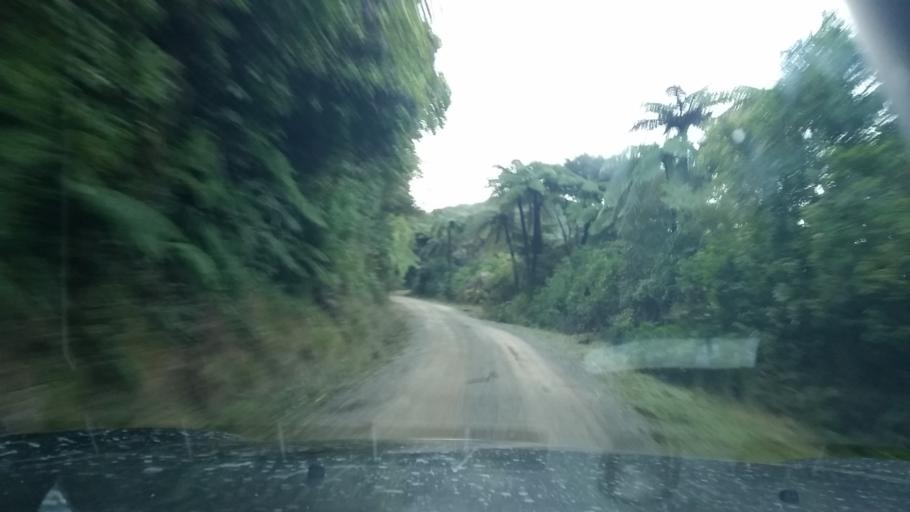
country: NZ
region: Marlborough
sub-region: Marlborough District
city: Picton
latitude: -41.1312
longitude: 174.1442
